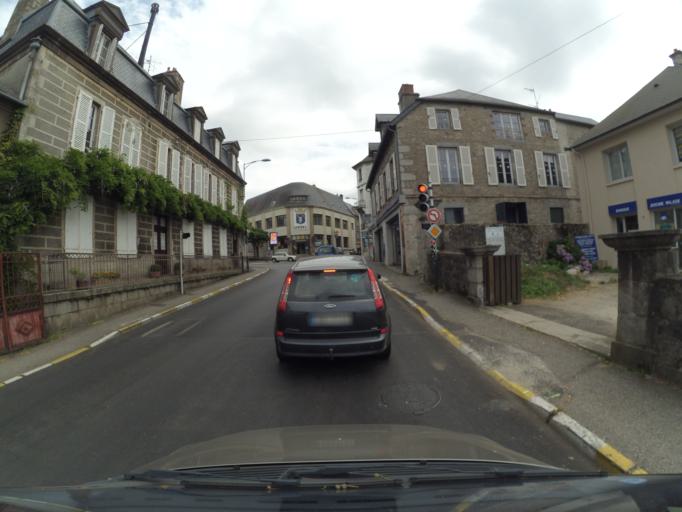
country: FR
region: Limousin
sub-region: Departement de la Correze
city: Ussel
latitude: 45.5463
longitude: 2.3078
